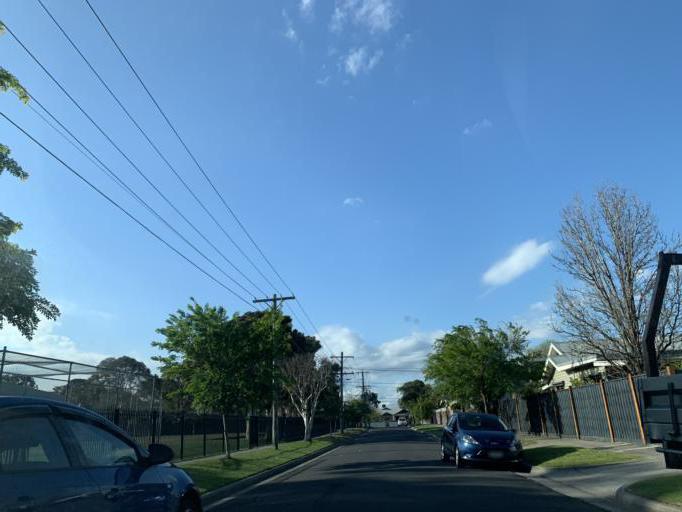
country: AU
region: Victoria
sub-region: Kingston
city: Mordialloc
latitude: -37.9936
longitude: 145.0850
